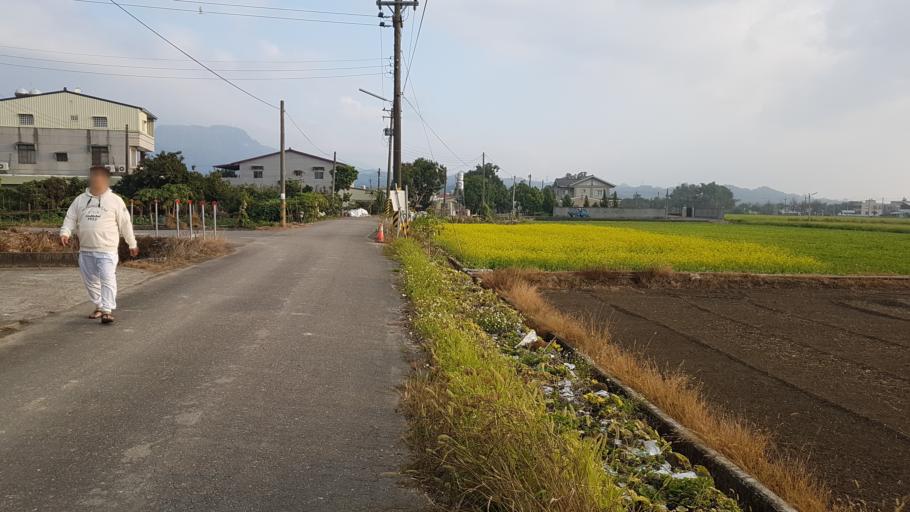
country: TW
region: Taiwan
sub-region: Chiayi
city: Jiayi Shi
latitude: 23.3721
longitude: 120.4547
